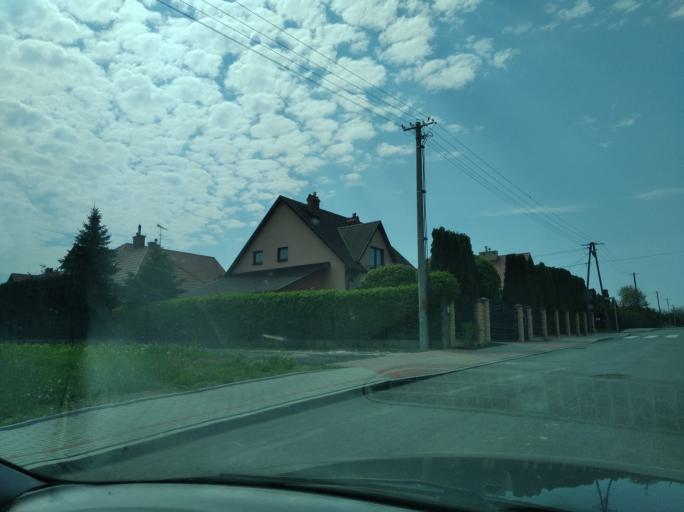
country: PL
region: Subcarpathian Voivodeship
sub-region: Powiat jaroslawski
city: Jaroslaw
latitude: 50.0032
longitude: 22.6811
